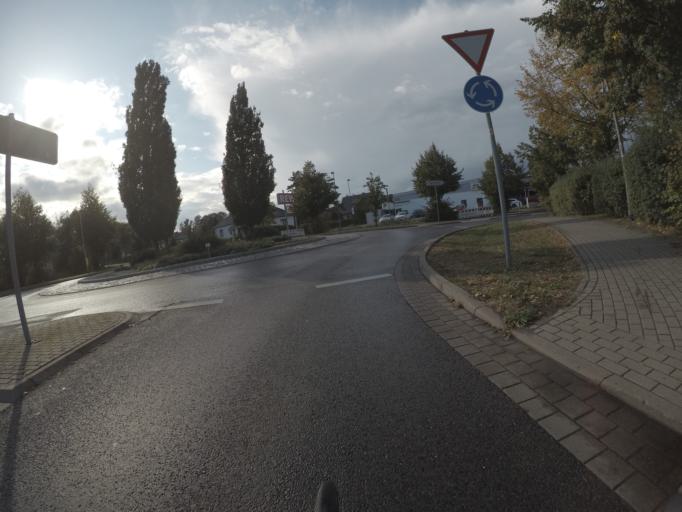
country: DE
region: Brandenburg
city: Petershagen
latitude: 52.5238
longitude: 13.7636
